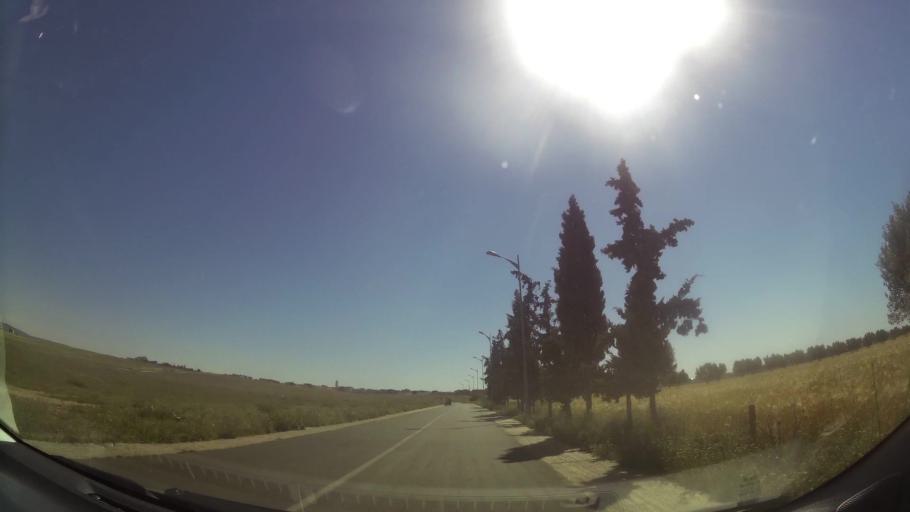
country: MA
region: Oriental
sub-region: Oujda-Angad
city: Oujda
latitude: 34.6948
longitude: -1.8618
